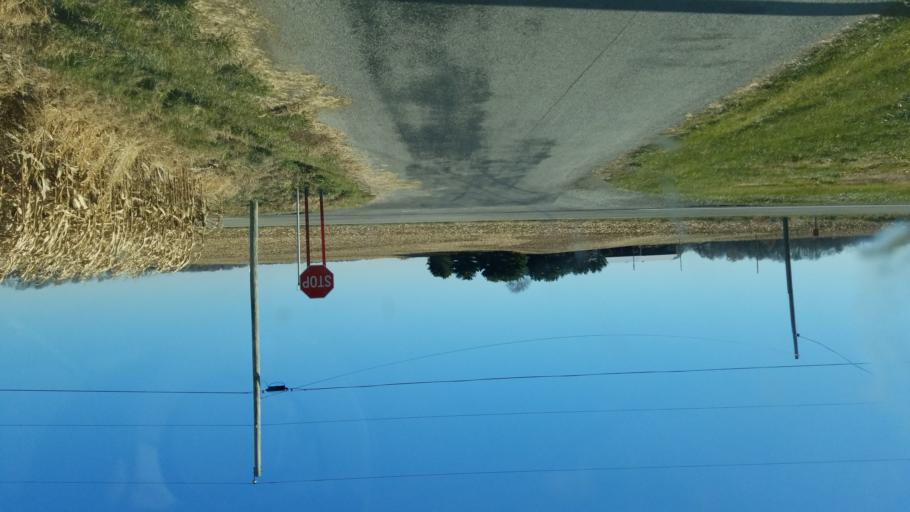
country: US
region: Ohio
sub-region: Crawford County
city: Bucyrus
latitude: 40.9025
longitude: -82.8544
